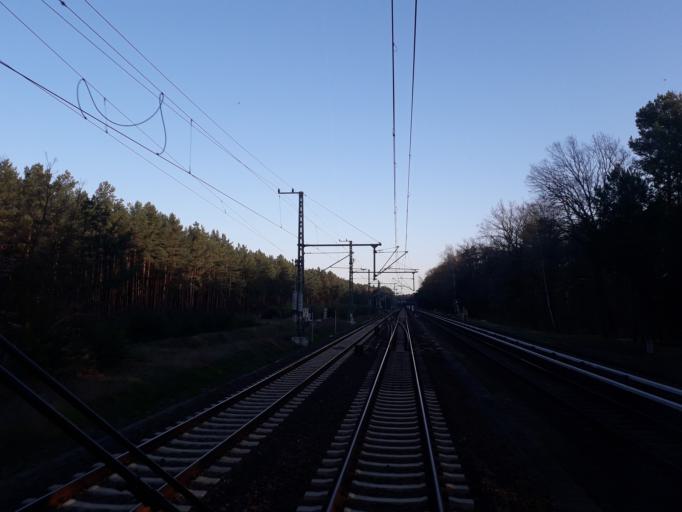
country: DE
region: Brandenburg
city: Zeuthen
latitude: 52.3864
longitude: 13.6055
